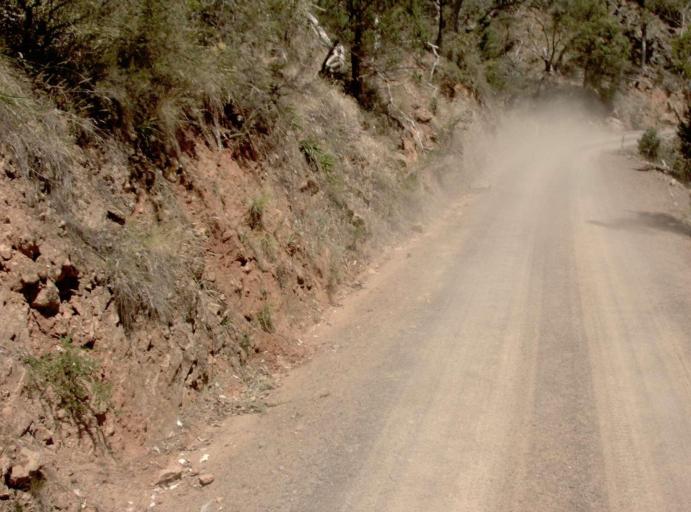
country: AU
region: New South Wales
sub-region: Snowy River
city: Jindabyne
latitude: -37.0832
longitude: 148.4519
